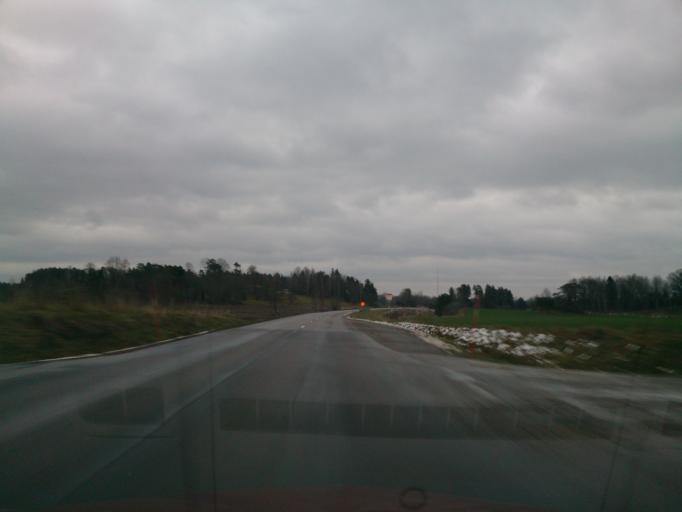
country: SE
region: OEstergoetland
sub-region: Linkopings Kommun
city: Linghem
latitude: 58.4128
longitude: 15.9043
